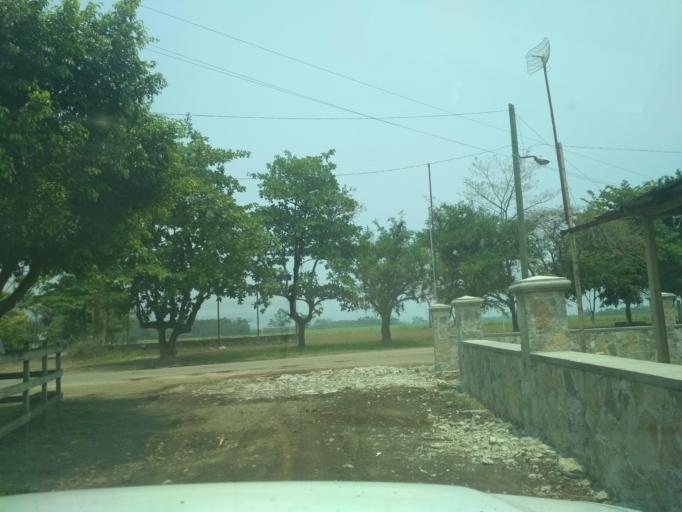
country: MX
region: Veracruz
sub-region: Tezonapa
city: Laguna Chica (Pueblo Nuevo)
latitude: 18.5112
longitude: -96.7371
